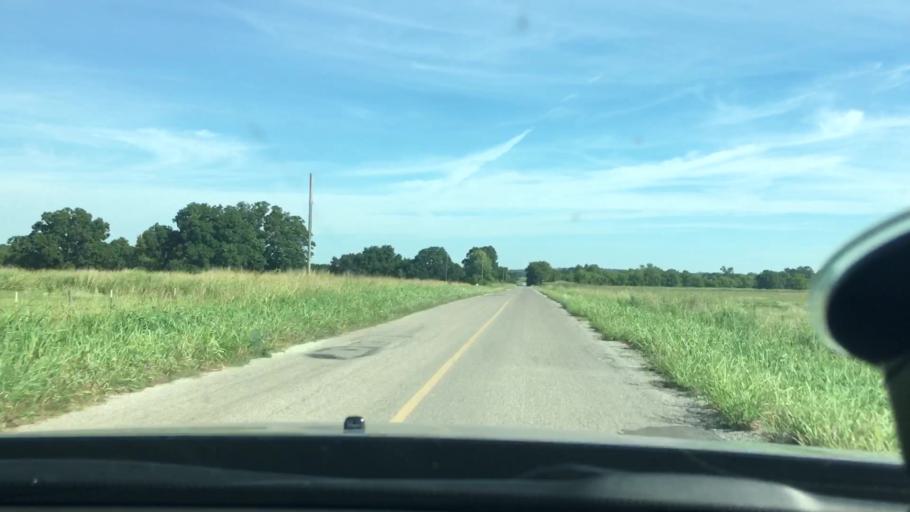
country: US
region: Oklahoma
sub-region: Carter County
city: Lone Grove
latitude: 34.3012
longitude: -97.2816
